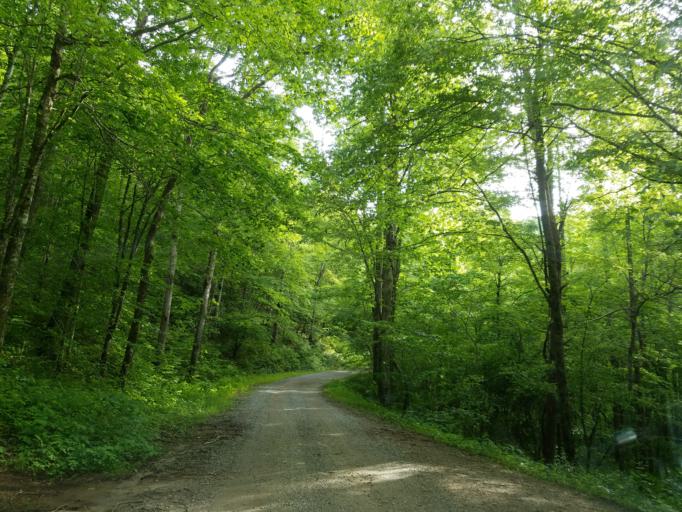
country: US
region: Georgia
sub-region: Union County
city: Blairsville
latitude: 34.7516
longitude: -84.0162
